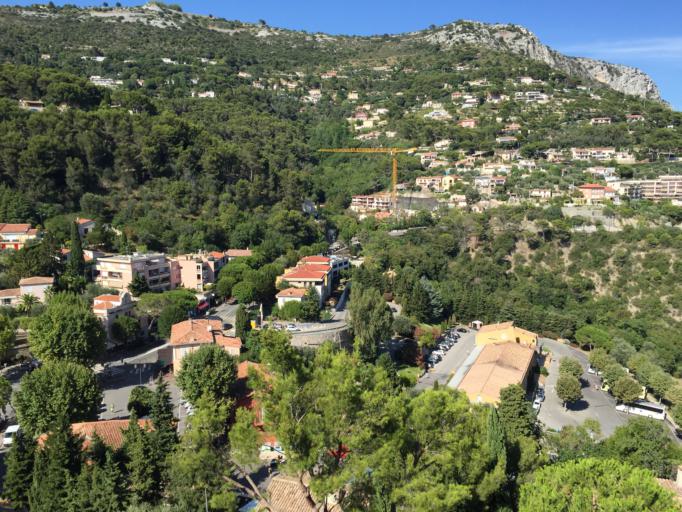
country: FR
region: Provence-Alpes-Cote d'Azur
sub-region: Departement des Alpes-Maritimes
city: Eze
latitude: 43.7287
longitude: 7.3616
